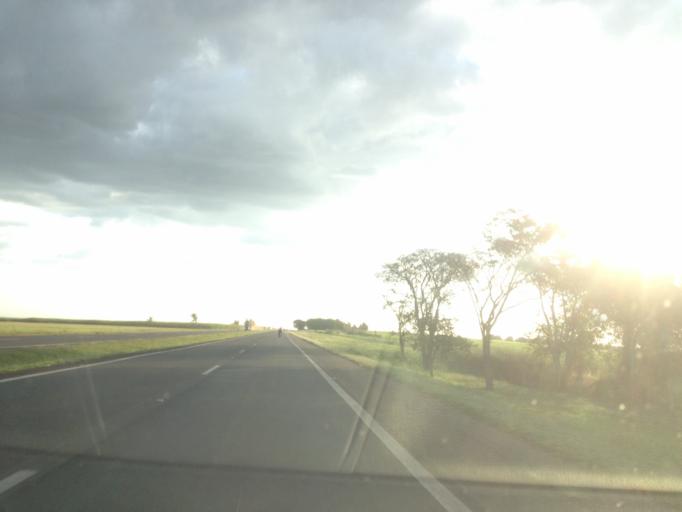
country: BR
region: Sao Paulo
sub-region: Jau
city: Jau
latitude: -22.2693
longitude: -48.4612
